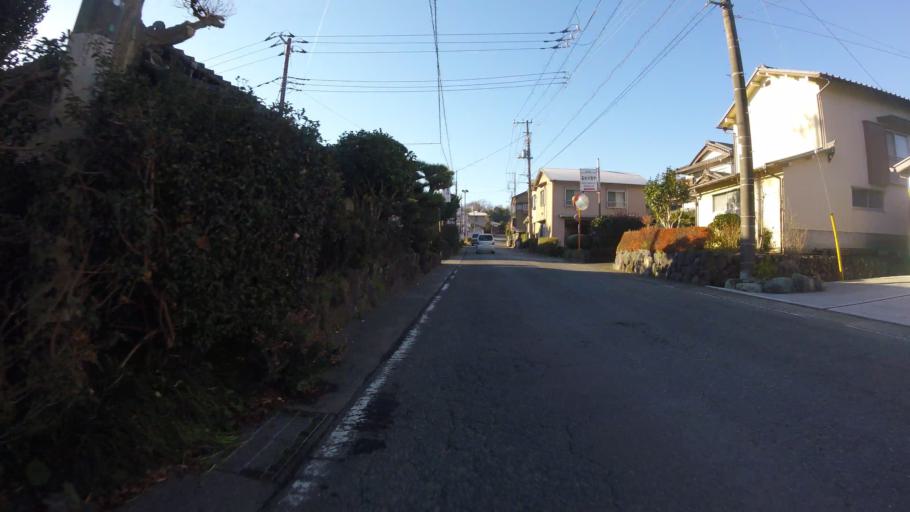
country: JP
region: Shizuoka
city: Ito
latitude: 34.9659
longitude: 138.9419
